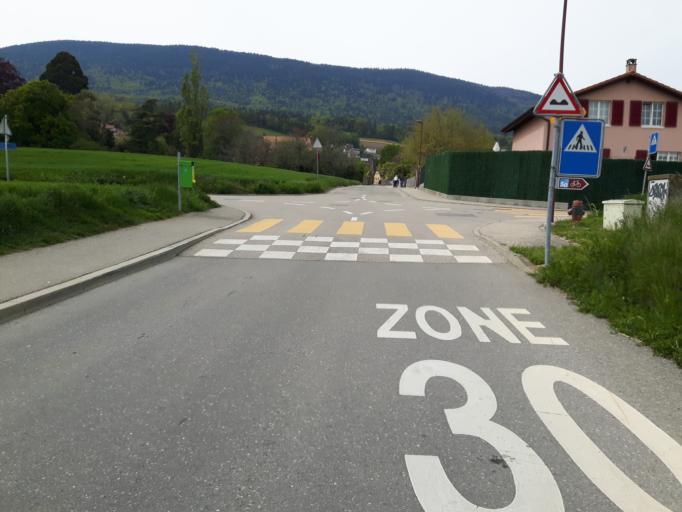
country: CH
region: Neuchatel
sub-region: Boudry District
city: Bevaix
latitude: 46.9284
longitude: 6.8172
